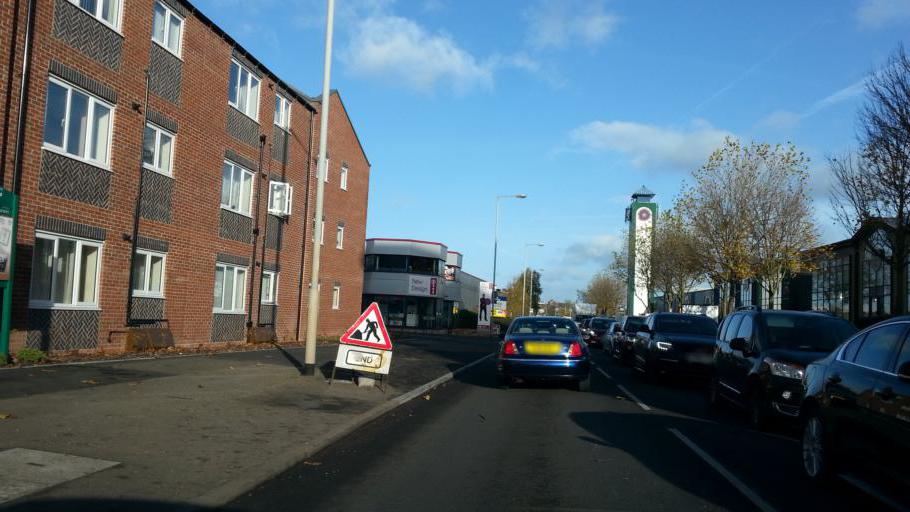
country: GB
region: England
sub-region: Staffordshire
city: Cannock
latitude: 52.6759
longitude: -2.0253
